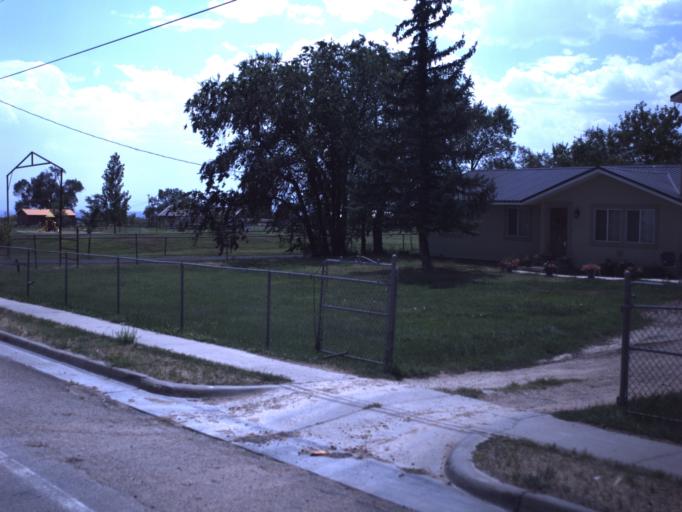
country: US
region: Utah
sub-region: Duchesne County
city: Roosevelt
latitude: 40.4309
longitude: -110.0301
